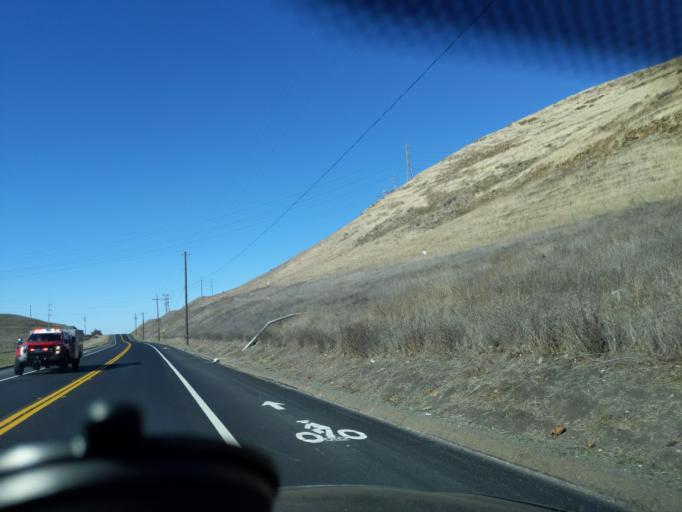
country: US
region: California
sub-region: Santa Clara County
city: Seven Trees
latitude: 37.2151
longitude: -121.7533
